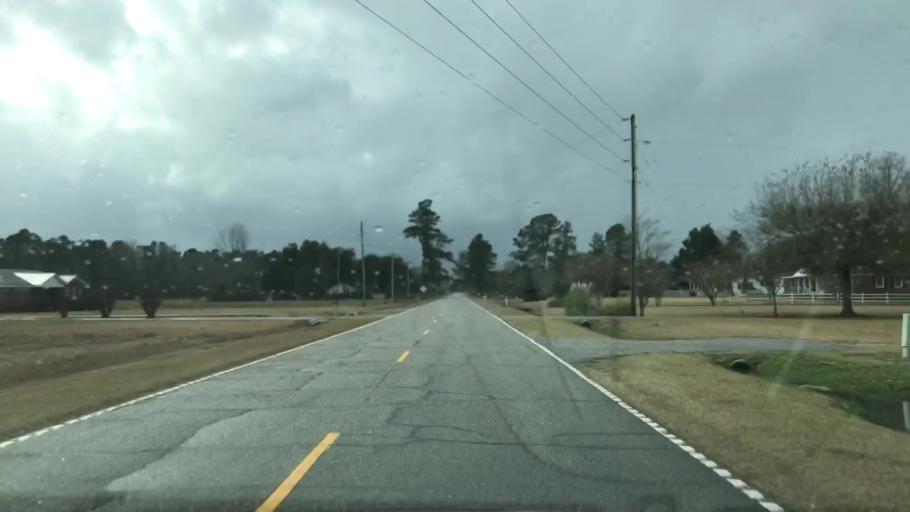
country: US
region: South Carolina
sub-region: Florence County
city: Johnsonville
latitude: 33.6739
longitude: -79.3937
